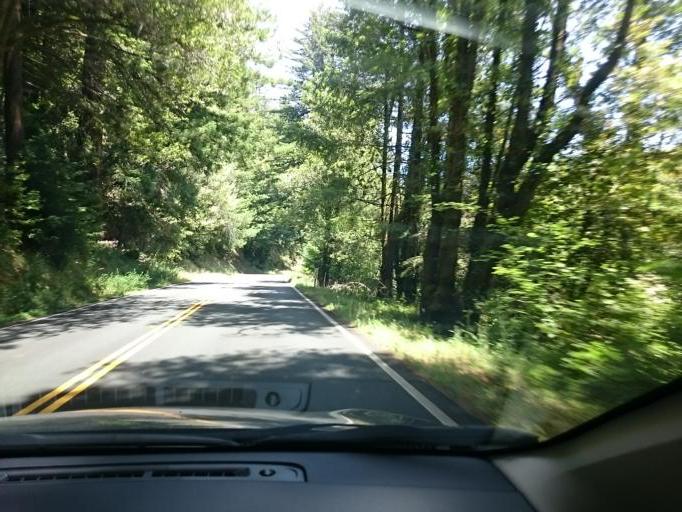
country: US
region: California
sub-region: Mendocino County
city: Fort Bragg
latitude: 39.1786
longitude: -123.6853
